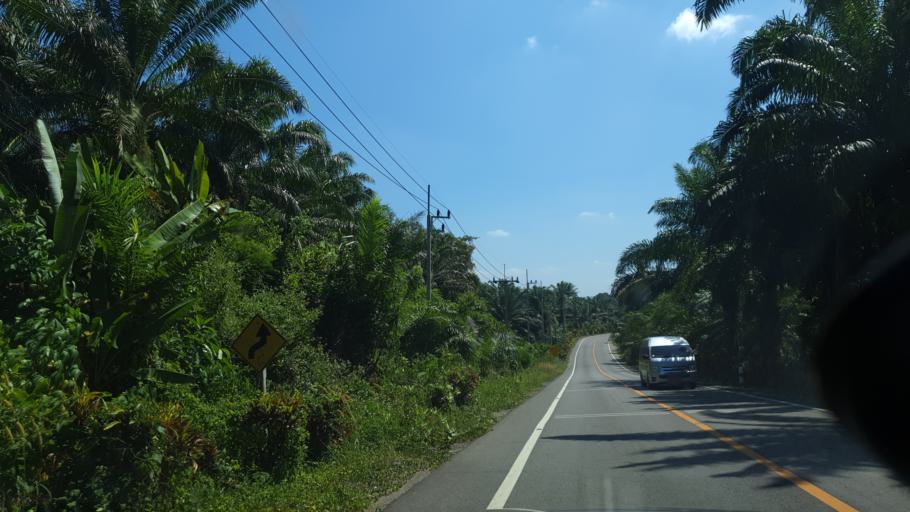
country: TH
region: Krabi
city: Khlong Thom
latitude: 7.9242
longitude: 99.2436
